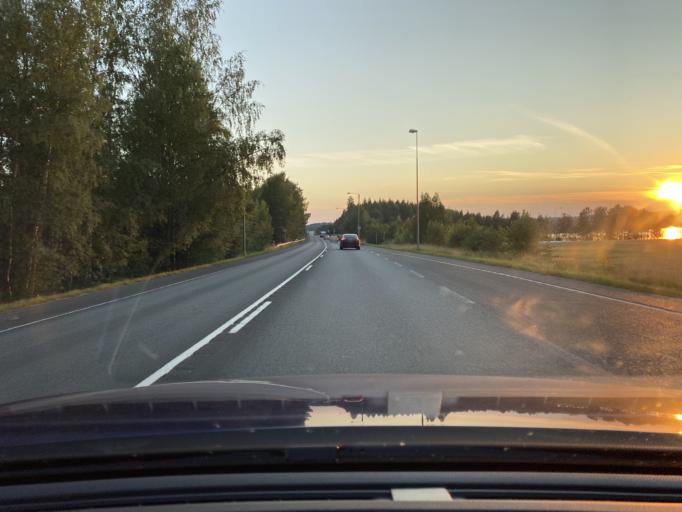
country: FI
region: Pirkanmaa
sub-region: Luoteis-Pirkanmaa
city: Ikaalinen
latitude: 61.7559
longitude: 23.0529
